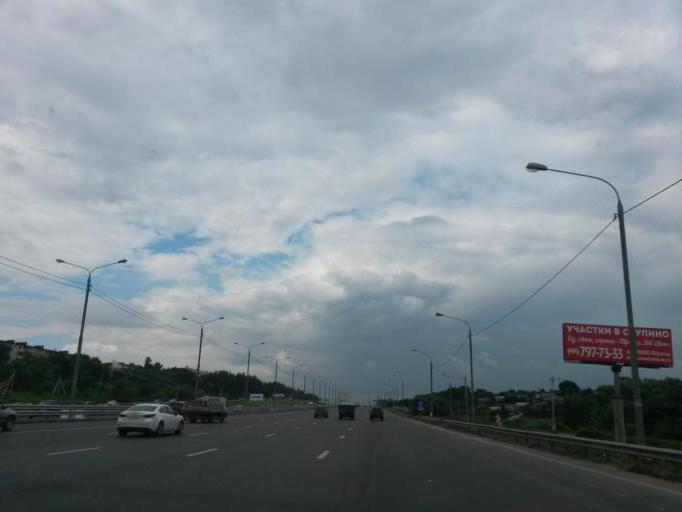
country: RU
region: Moskovskaya
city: Shcherbinka
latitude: 55.4697
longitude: 37.6180
